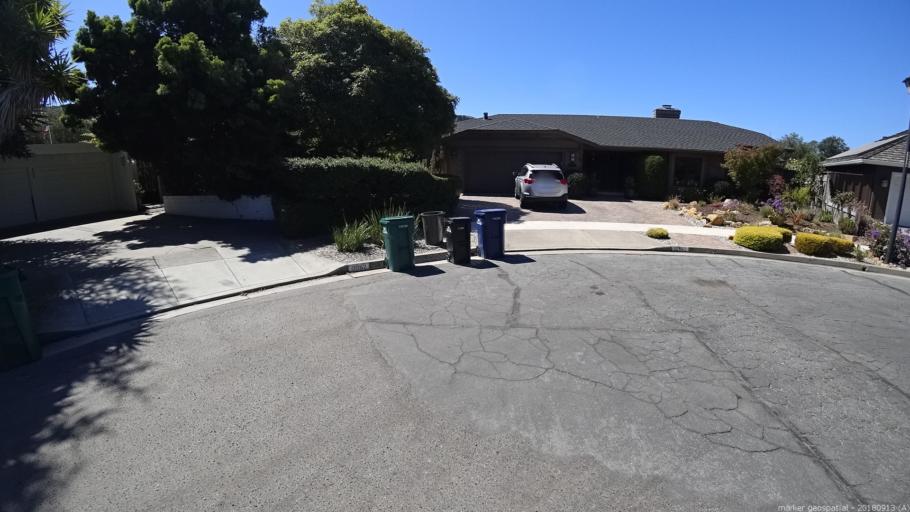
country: US
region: California
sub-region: Monterey County
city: Del Rey Oaks
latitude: 36.5316
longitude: -121.8557
